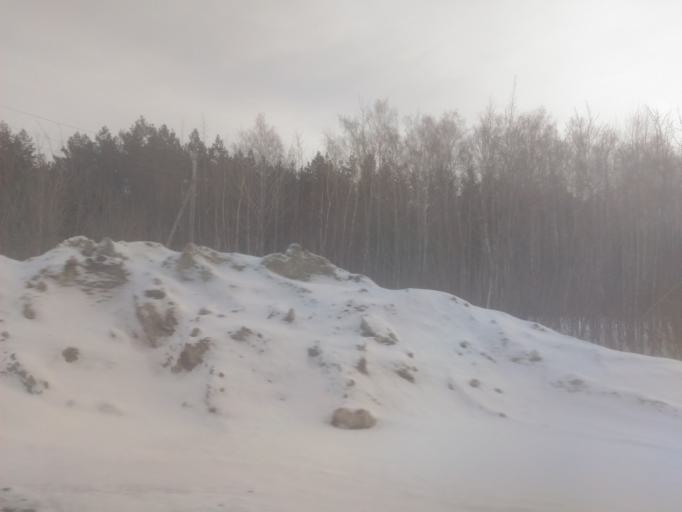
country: RU
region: Ulyanovsk
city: Isheyevka
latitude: 54.3757
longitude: 48.3093
